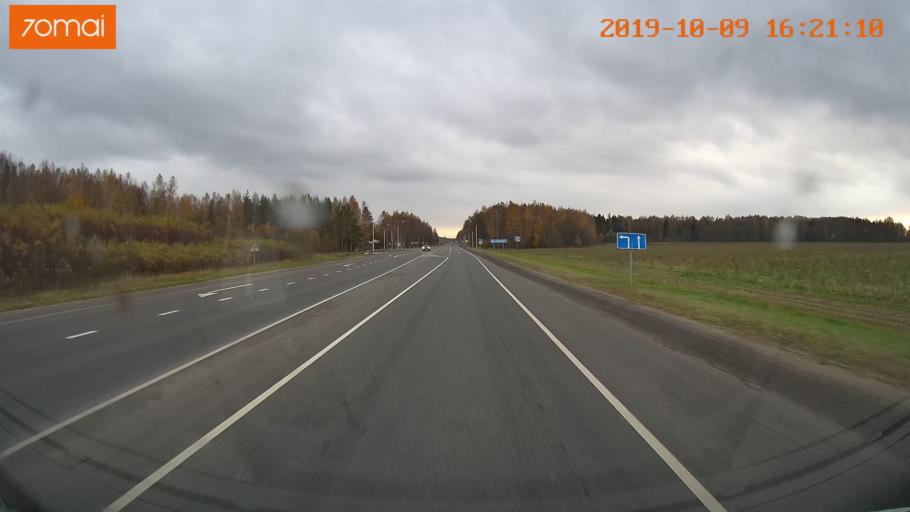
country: RU
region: Kostroma
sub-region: Kostromskoy Rayon
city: Kostroma
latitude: 57.6962
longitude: 40.8900
